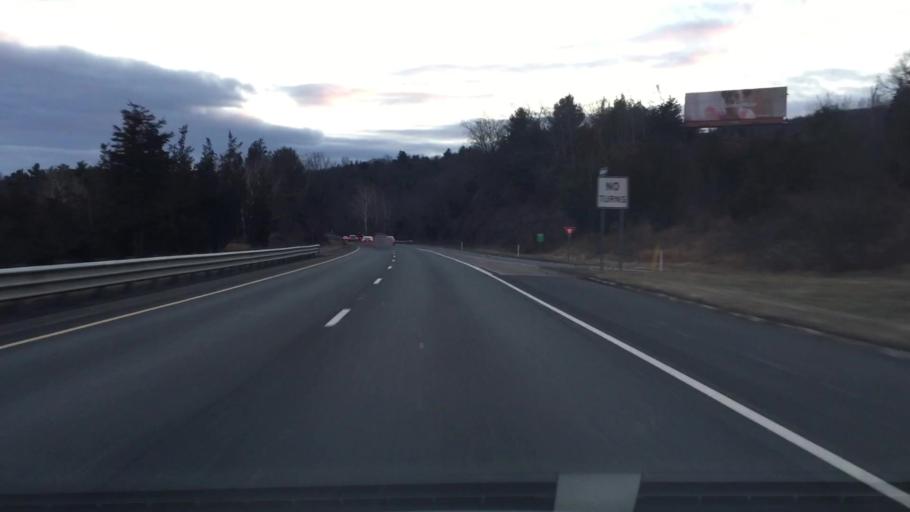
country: US
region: Massachusetts
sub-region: Hampshire County
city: South Hadley
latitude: 42.2538
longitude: -72.6213
